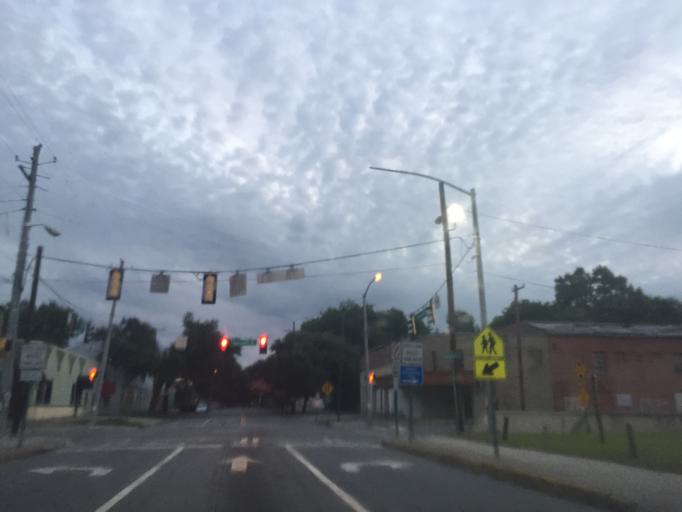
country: US
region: Georgia
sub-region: Chatham County
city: Savannah
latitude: 32.0649
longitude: -81.0893
